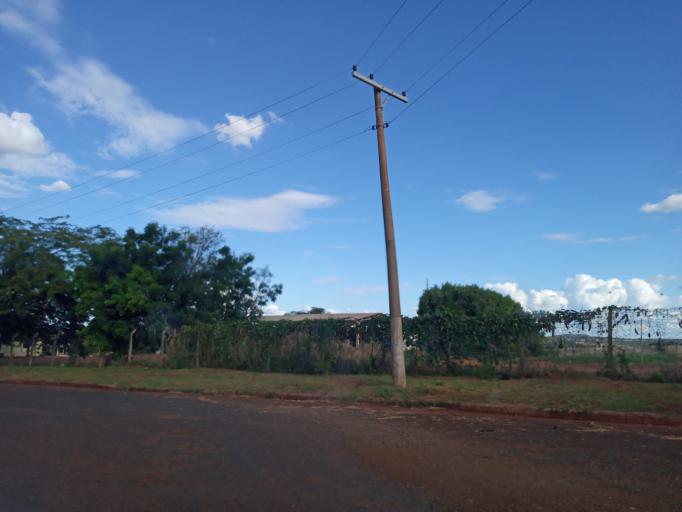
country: BR
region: Minas Gerais
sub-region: Ituiutaba
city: Ituiutaba
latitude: -18.9643
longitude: -49.4969
